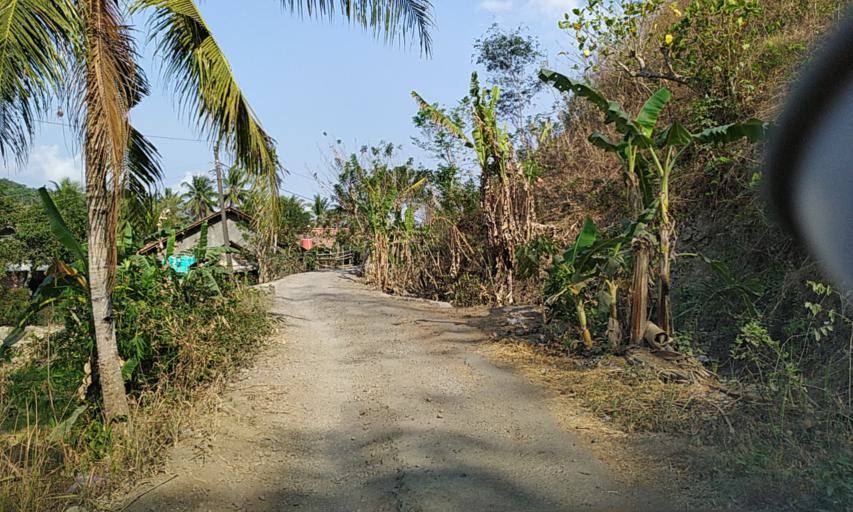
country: ID
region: Central Java
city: Jambuluwuk
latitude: -7.3155
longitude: 108.8765
